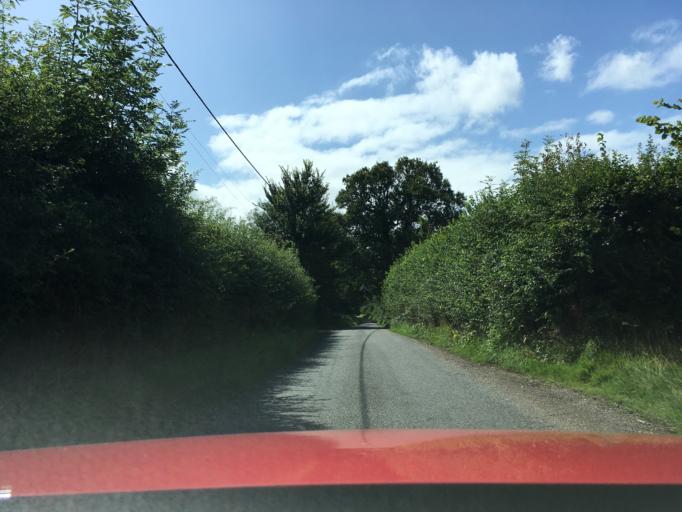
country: GB
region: England
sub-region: West Berkshire
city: Wickham
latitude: 51.4226
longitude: -1.4123
